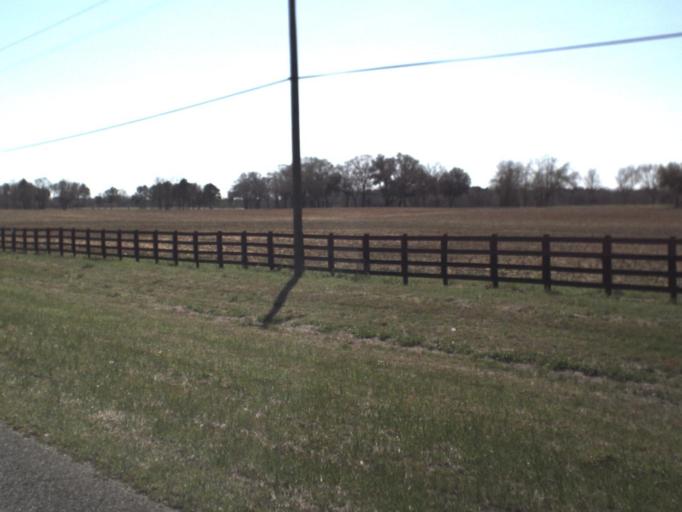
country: US
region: Florida
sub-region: Jackson County
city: Graceville
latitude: 30.9370
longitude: -85.3903
